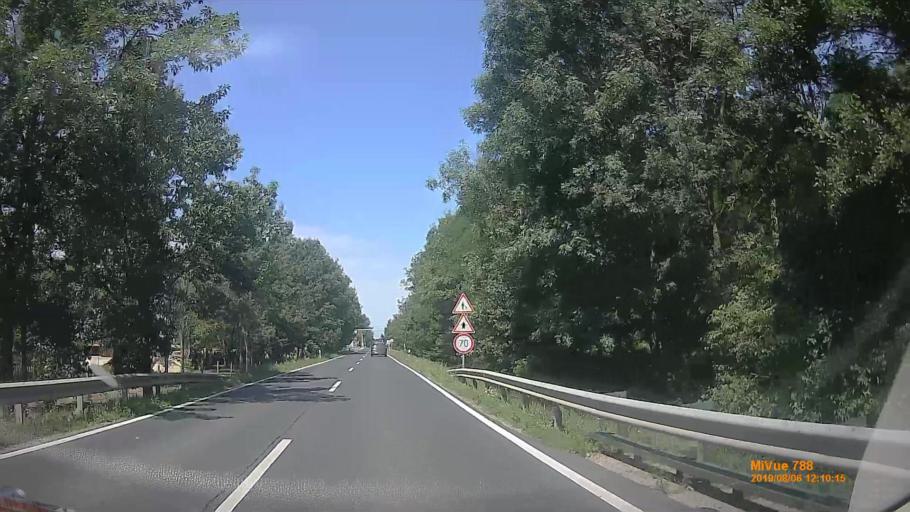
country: HU
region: Vas
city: Vasvar
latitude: 47.1022
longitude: 16.8738
